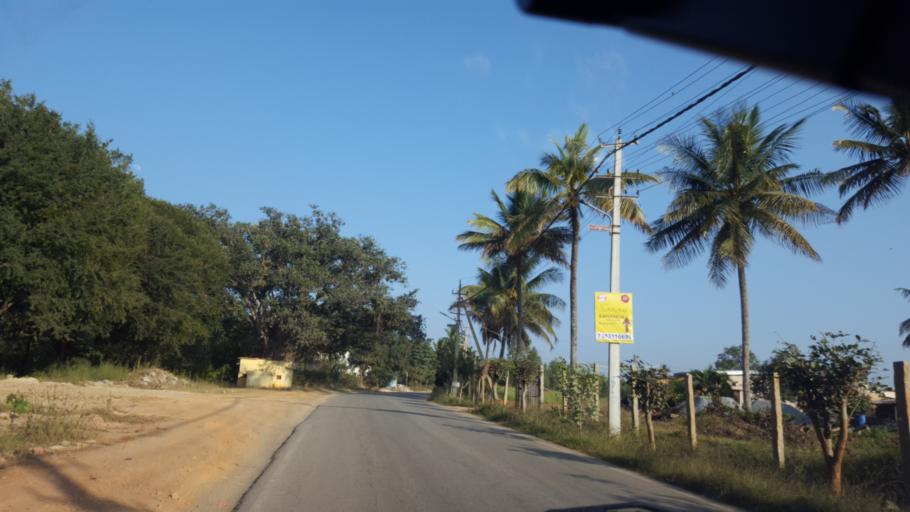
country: IN
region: Karnataka
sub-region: Bangalore Rural
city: Hoskote
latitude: 12.9147
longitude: 77.7673
